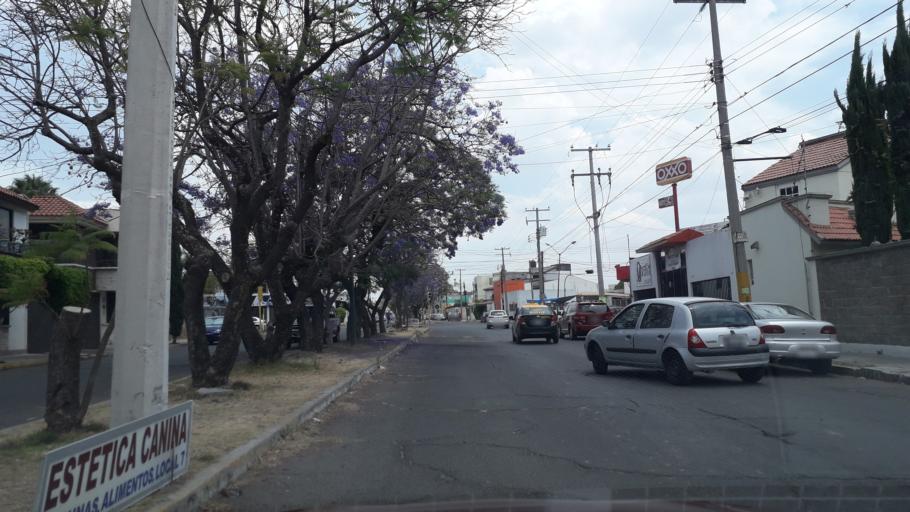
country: MX
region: Puebla
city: Puebla
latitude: 19.0179
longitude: -98.1959
